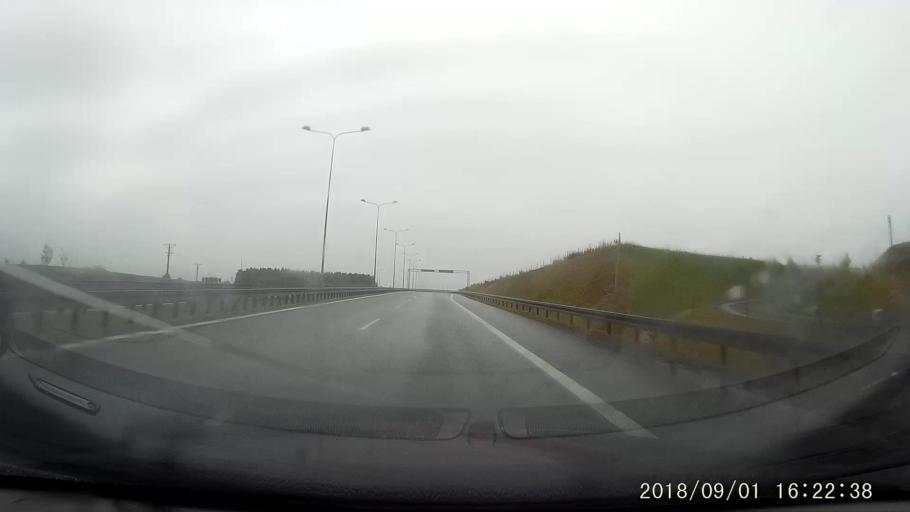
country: PL
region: Lubusz
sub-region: Powiat swiebodzinski
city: Swiebodzin
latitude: 52.3232
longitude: 15.5519
